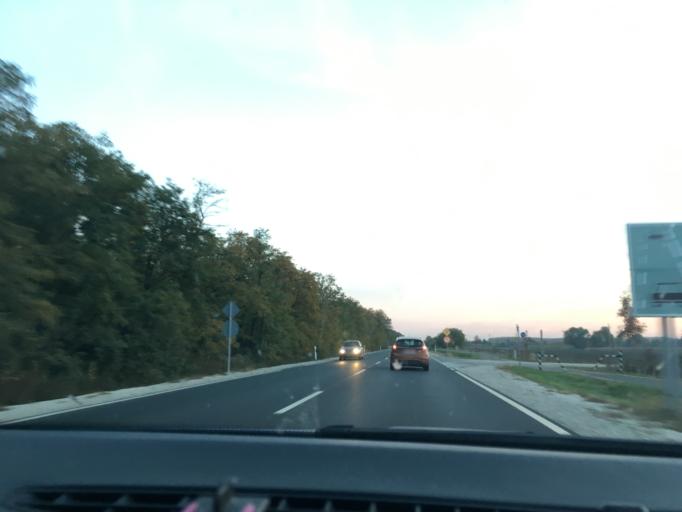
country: HU
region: Hajdu-Bihar
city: Hajduhadhaz
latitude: 47.6328
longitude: 21.6594
